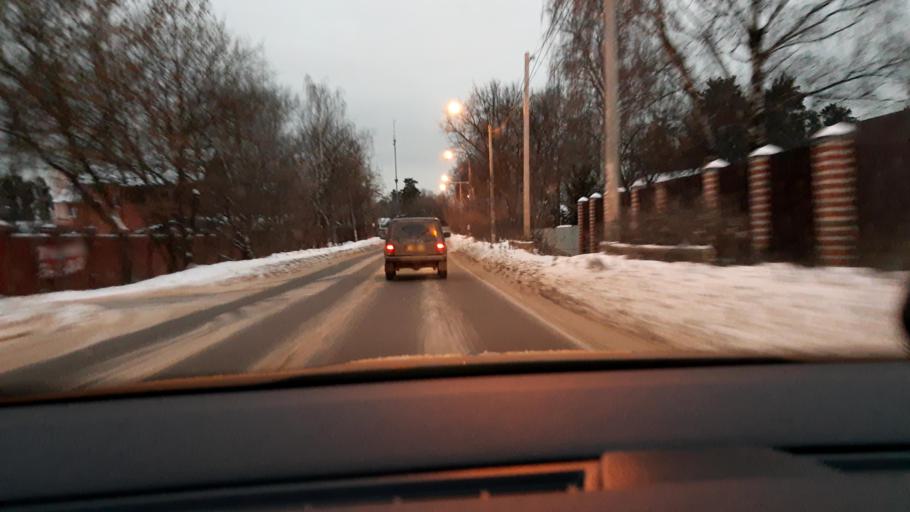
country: RU
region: Moskovskaya
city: Tomilino
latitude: 55.6452
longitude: 37.9522
